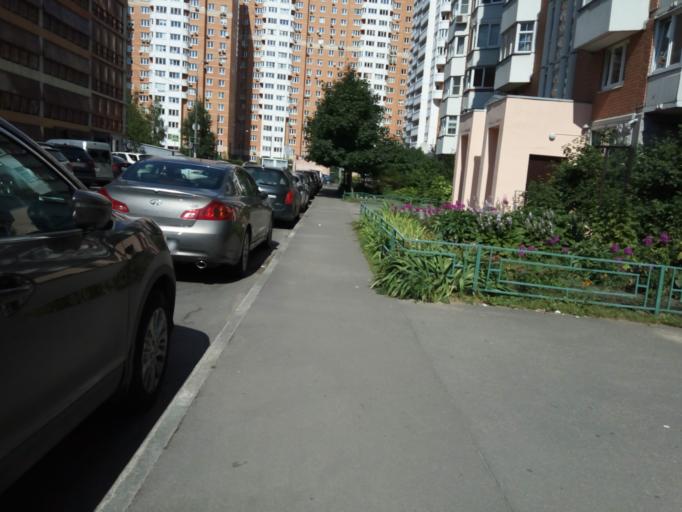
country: RU
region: Moscow
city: Sokol
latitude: 55.7806
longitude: 37.5328
